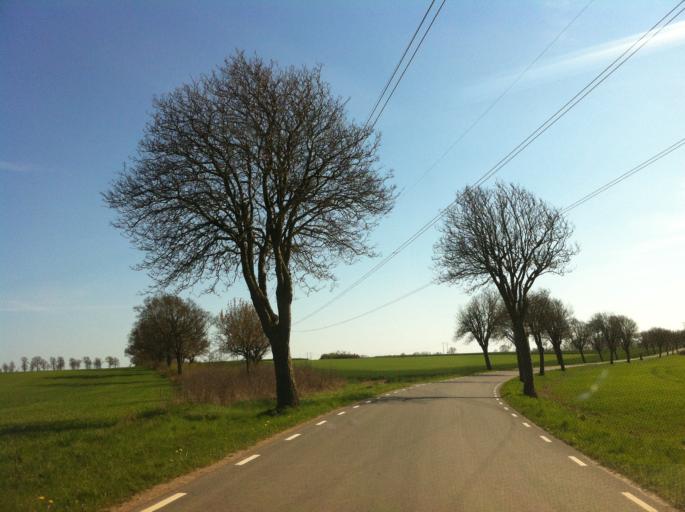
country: SE
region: Skane
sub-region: Svalovs Kommun
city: Kagerod
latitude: 56.0007
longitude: 13.0900
